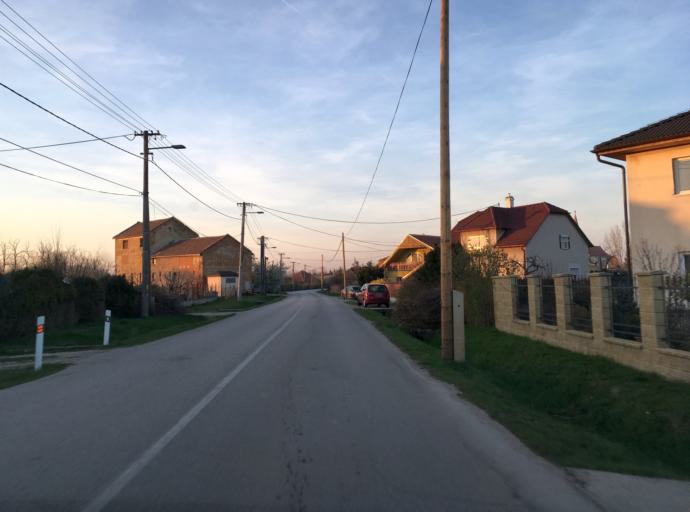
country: SK
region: Nitriansky
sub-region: Okres Komarno
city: Hurbanovo
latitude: 47.9016
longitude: 18.3073
